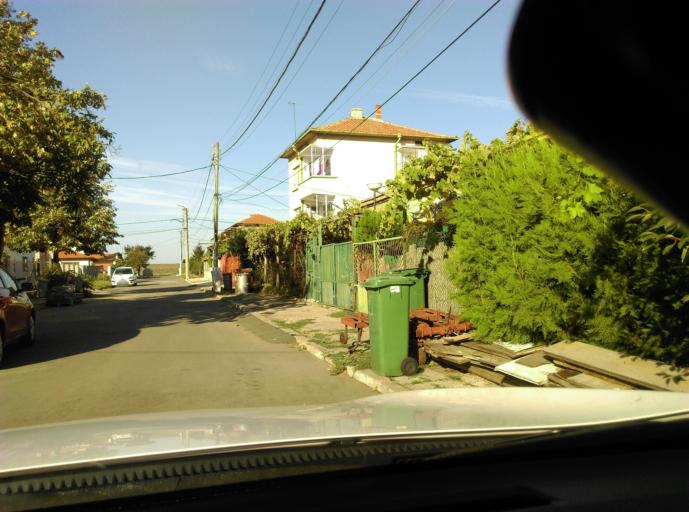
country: BG
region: Burgas
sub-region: Obshtina Kameno
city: Kameno
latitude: 42.6004
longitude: 27.3831
